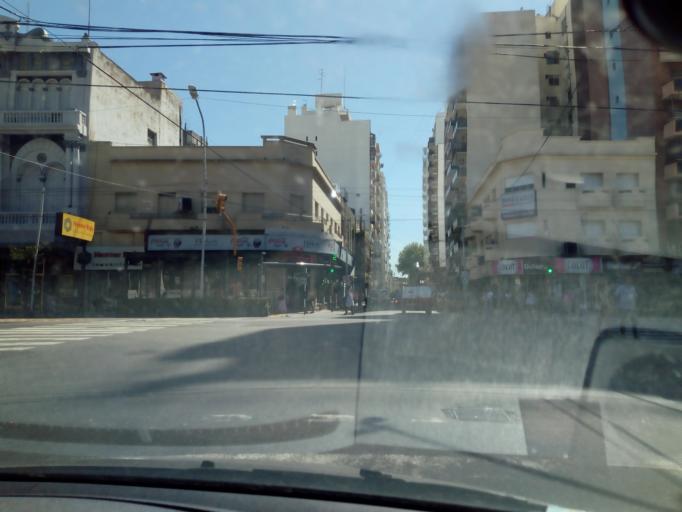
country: AR
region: Buenos Aires
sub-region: Partido de Avellaneda
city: Avellaneda
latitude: -34.6631
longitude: -58.3645
